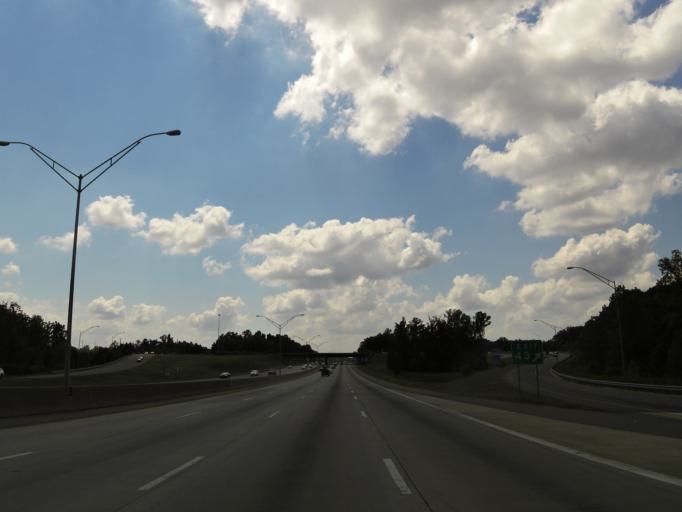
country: US
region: North Carolina
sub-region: Mecklenburg County
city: Charlotte
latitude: 35.2943
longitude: -80.7669
